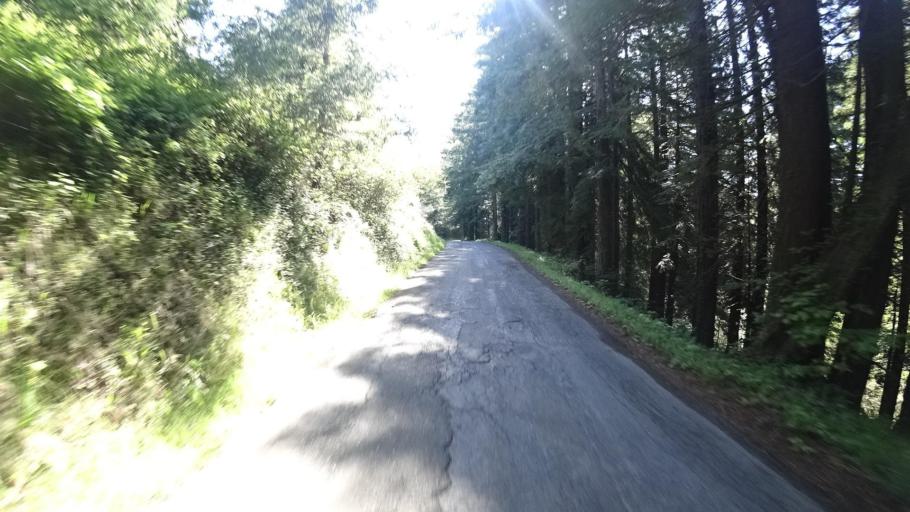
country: US
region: California
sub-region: Humboldt County
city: Rio Dell
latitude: 40.4607
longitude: -124.0454
